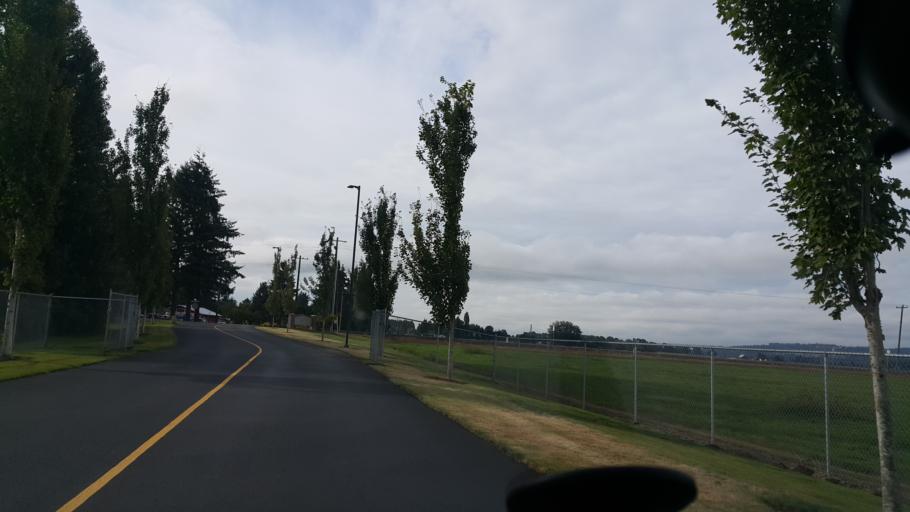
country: US
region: Washington
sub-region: Cowlitz County
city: Woodland
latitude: 45.9286
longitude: -122.7685
